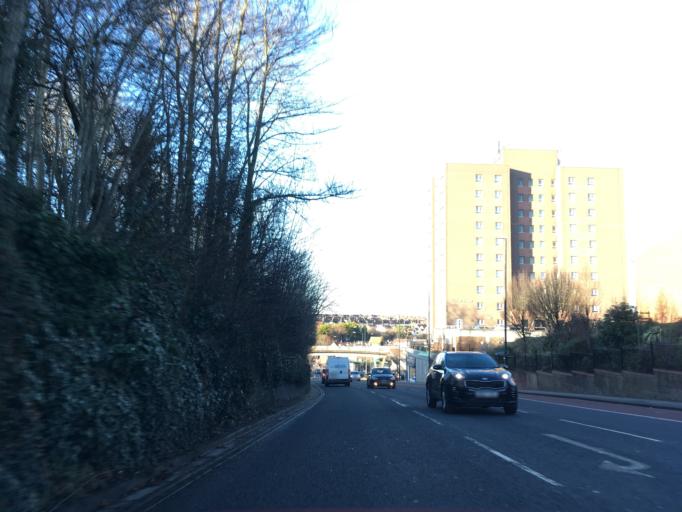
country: GB
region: England
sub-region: Bath and North East Somerset
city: Whitchurch
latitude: 51.4324
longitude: -2.5461
